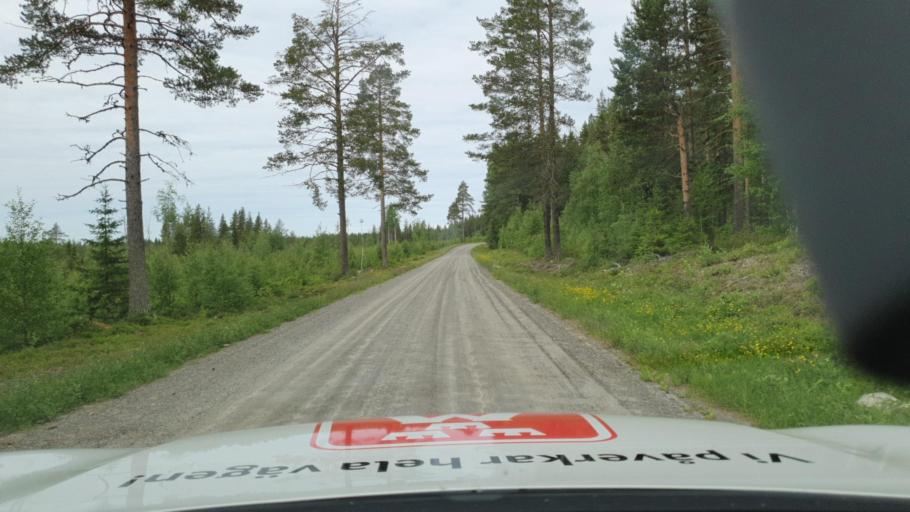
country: SE
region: Vaesterbotten
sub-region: Skelleftea Kommun
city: Langsele
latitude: 64.4772
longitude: 20.2092
